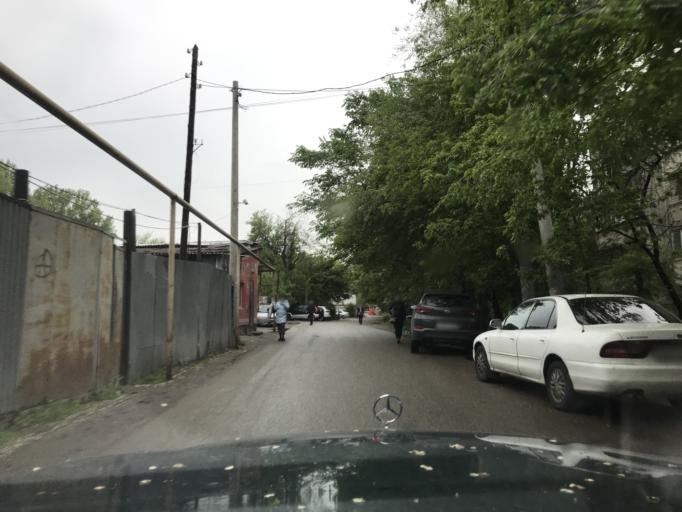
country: KZ
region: Almaty Qalasy
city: Almaty
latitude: 43.2091
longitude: 76.8817
